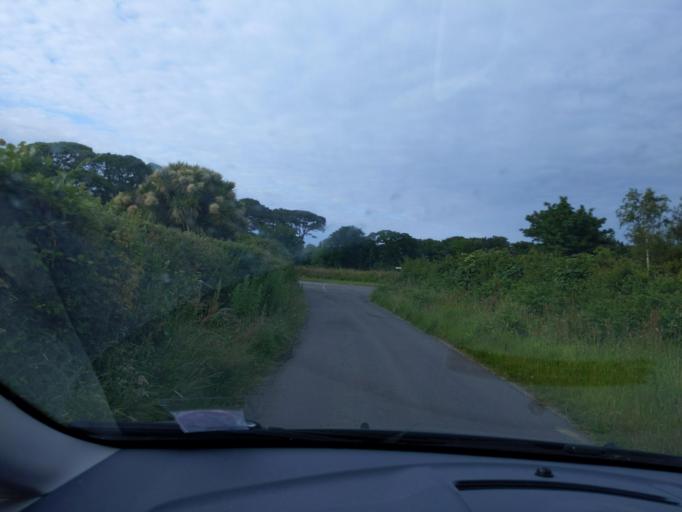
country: IM
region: Ramsey
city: Ramsey
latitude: 54.3639
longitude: -4.4379
